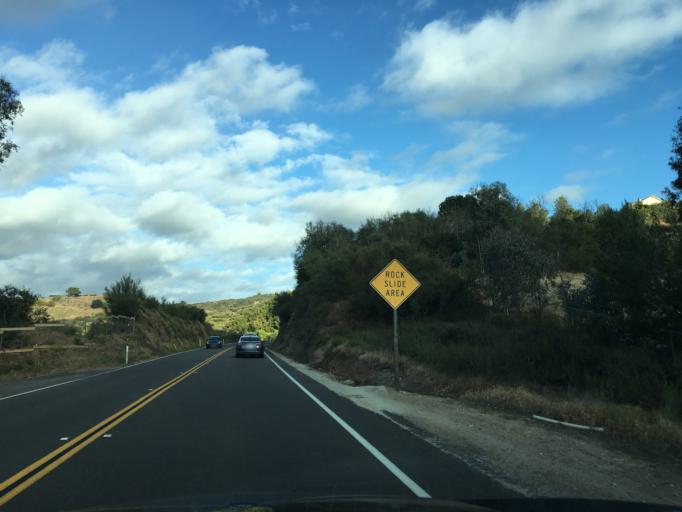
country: US
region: California
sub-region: San Diego County
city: Valley Center
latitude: 33.2485
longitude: -117.0563
